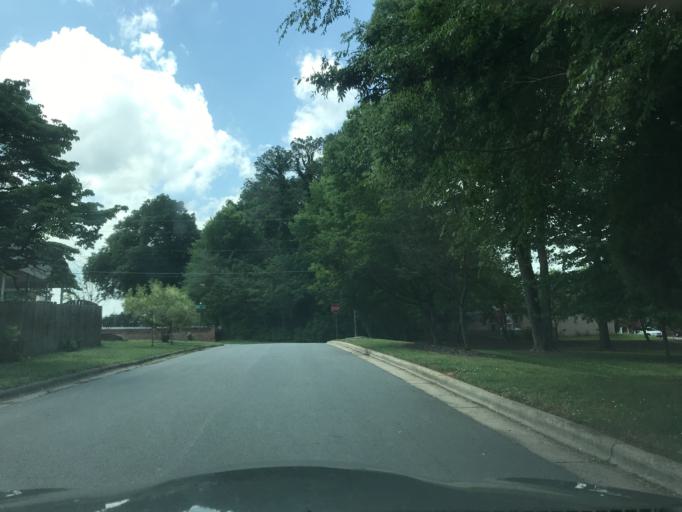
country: US
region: North Carolina
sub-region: Wake County
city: Raleigh
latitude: 35.7749
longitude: -78.6189
